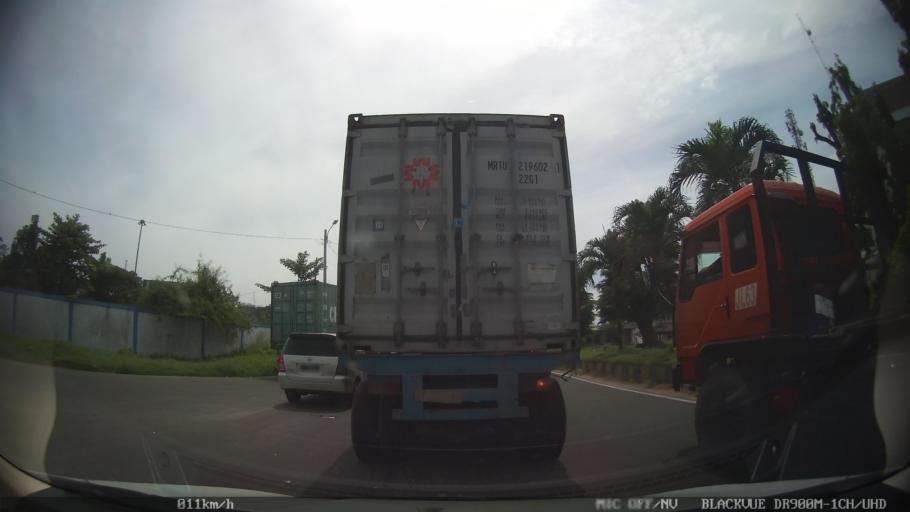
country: ID
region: North Sumatra
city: Belawan
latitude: 3.7816
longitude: 98.6938
